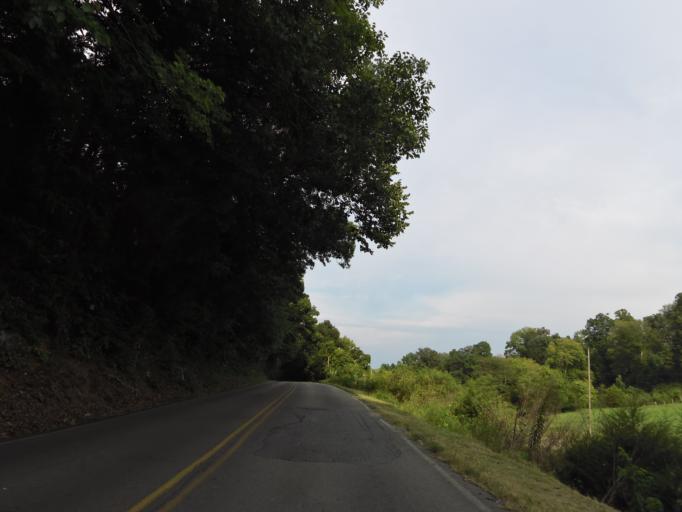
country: US
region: Tennessee
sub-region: Dickson County
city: Burns
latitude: 36.0294
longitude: -87.3258
